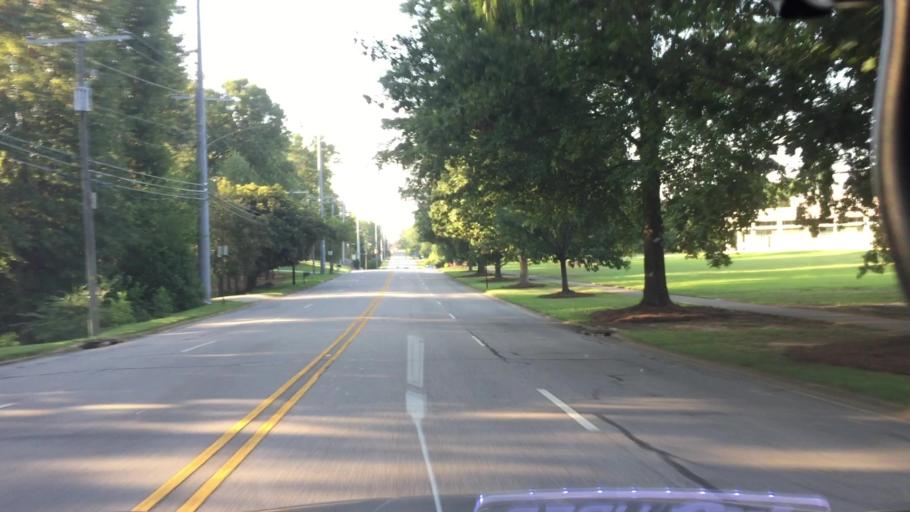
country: US
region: Alabama
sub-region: Lee County
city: Auburn
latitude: 32.5966
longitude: -85.4648
